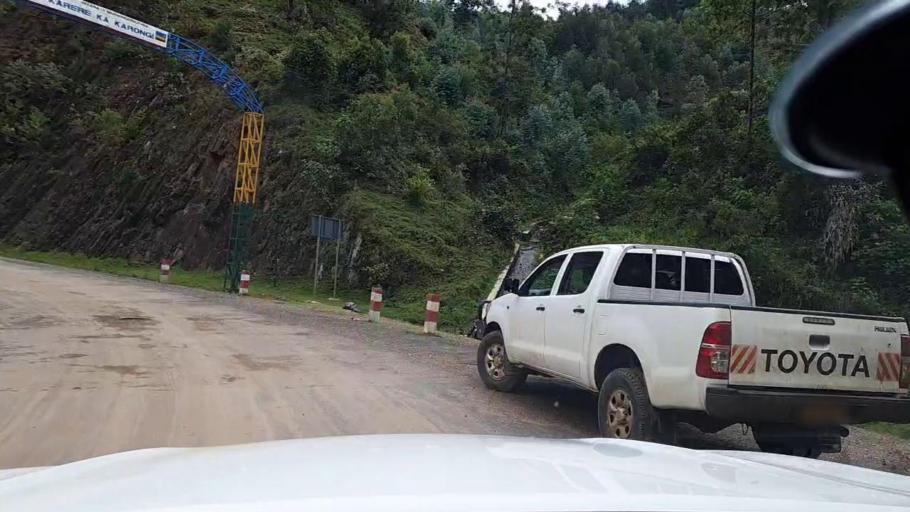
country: RW
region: Southern Province
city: Gitarama
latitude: -2.0637
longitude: 29.5584
